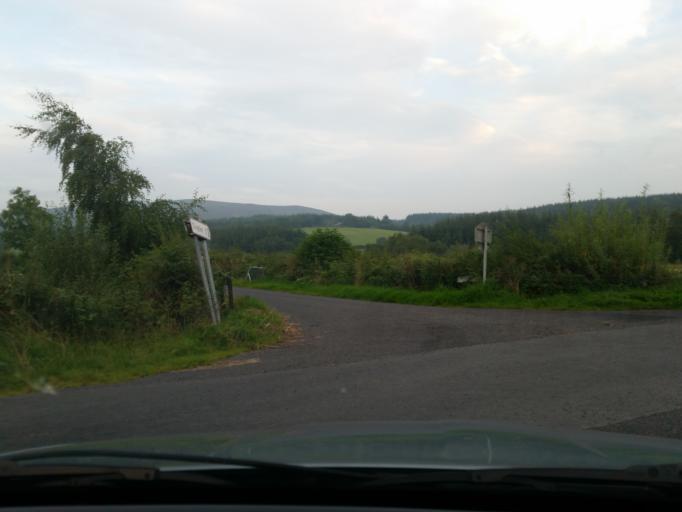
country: GB
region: Northern Ireland
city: Fivemiletown
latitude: 54.3653
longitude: -7.2670
